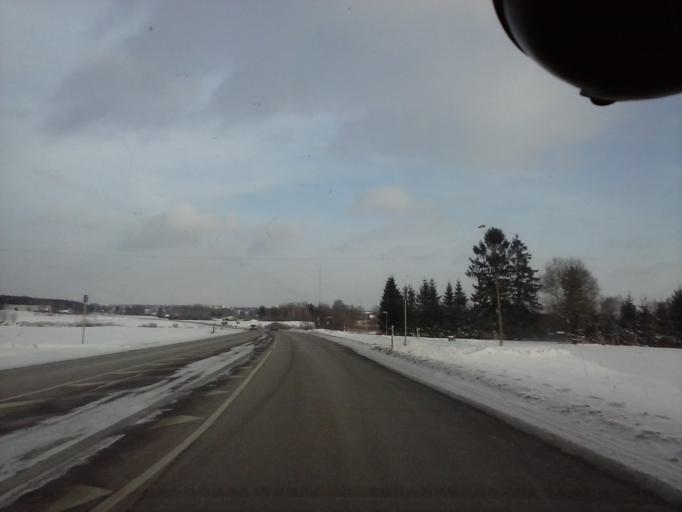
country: EE
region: Tartu
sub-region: Noo vald
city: Noo
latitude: 58.3538
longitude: 26.5994
